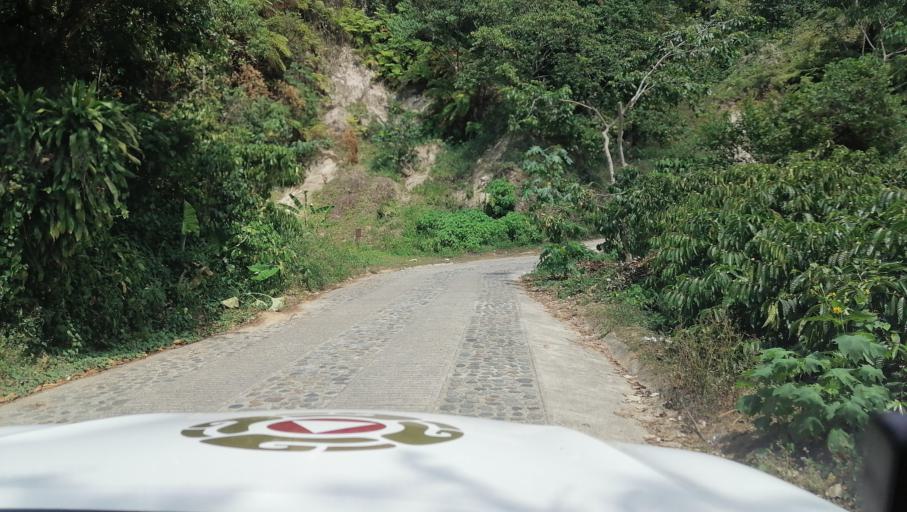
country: MX
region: Chiapas
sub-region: Tapachula
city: Canton Villaflor
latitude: 15.1380
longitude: -92.2881
